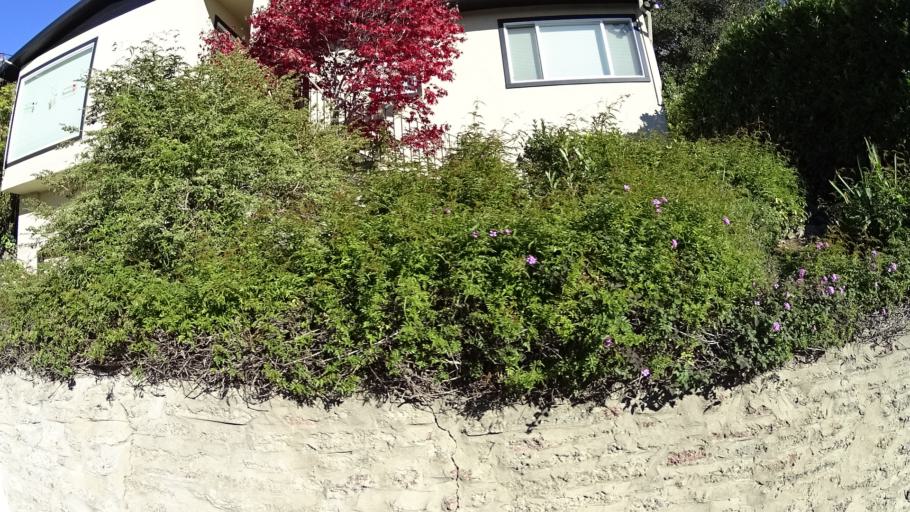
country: US
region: California
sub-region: Alameda County
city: Piedmont
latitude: 37.8284
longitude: -122.2297
